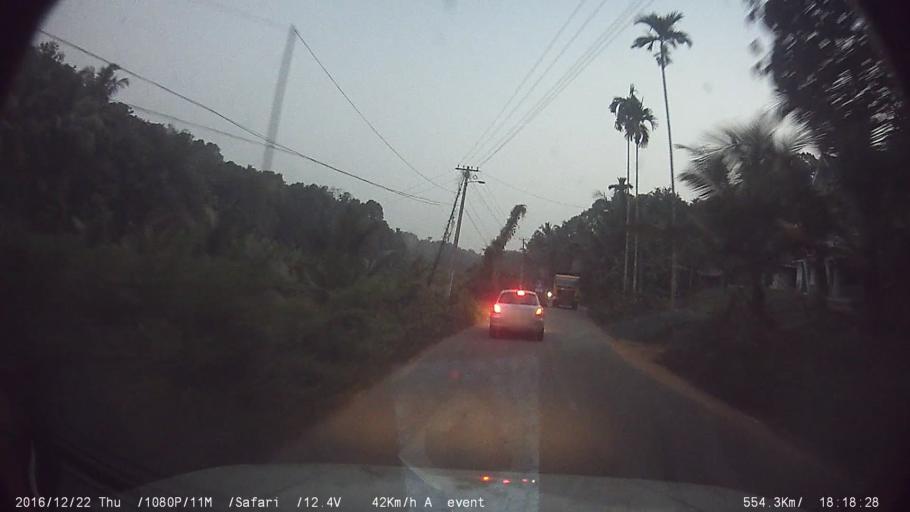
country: IN
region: Kerala
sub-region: Kottayam
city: Palackattumala
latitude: 9.7540
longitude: 76.6089
